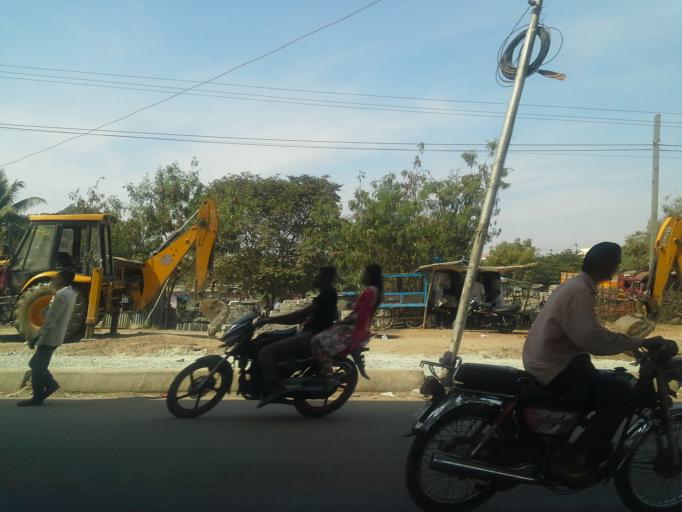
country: IN
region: Telangana
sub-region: Hyderabad
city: Hyderabad
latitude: 17.3620
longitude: 78.4278
